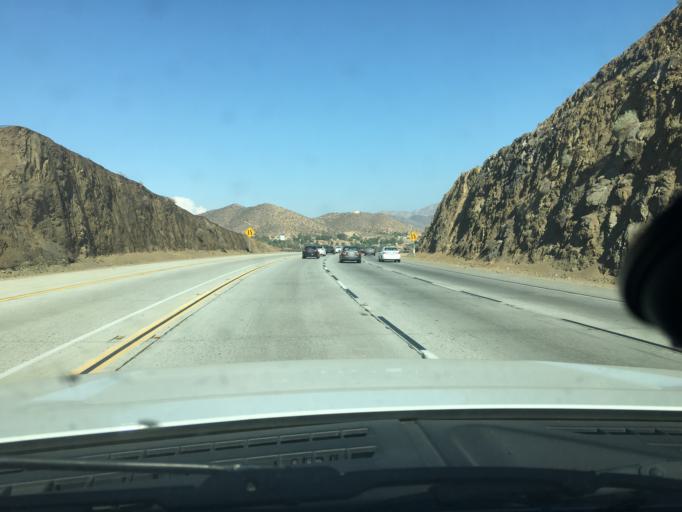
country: US
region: California
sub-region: Los Angeles County
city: Acton
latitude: 34.4932
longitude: -118.1736
